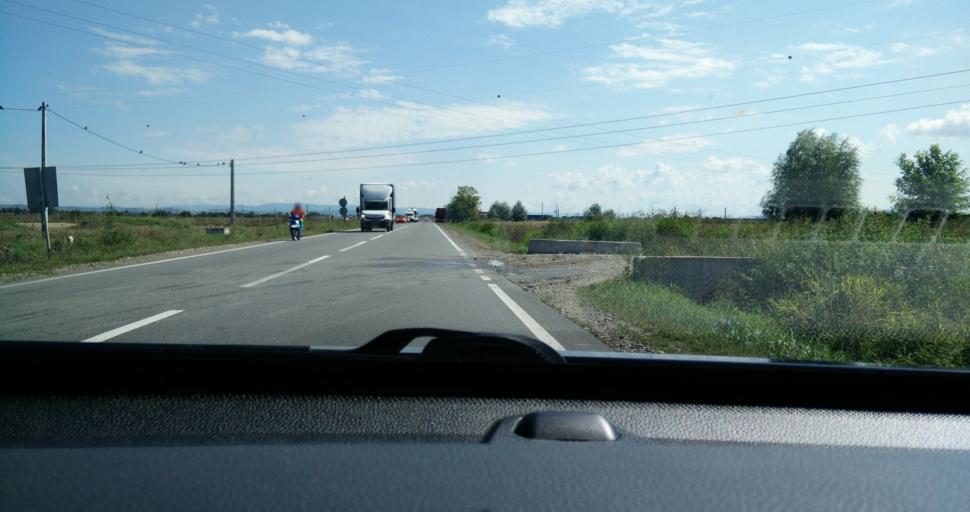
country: RO
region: Bihor
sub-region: Comuna Osorheiu
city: Osorheiu
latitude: 47.0504
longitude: 22.0533
